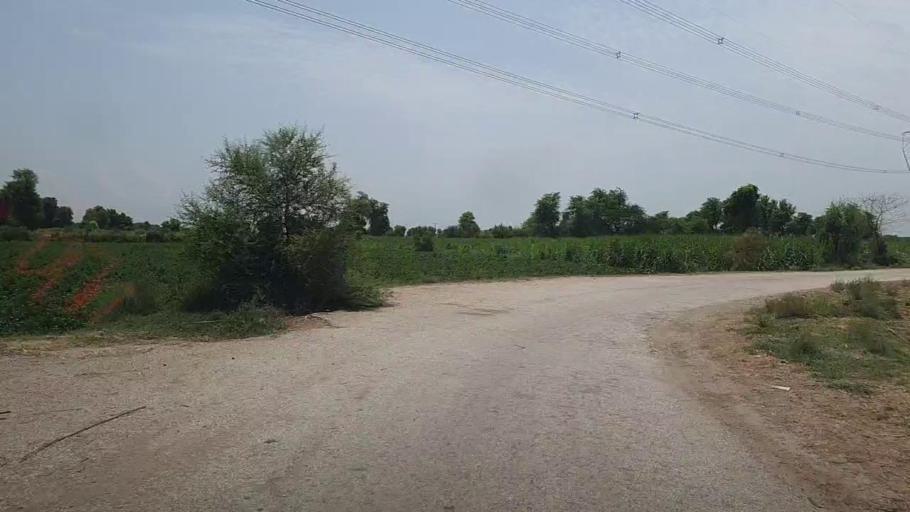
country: PK
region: Sindh
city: Pano Aqil
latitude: 27.8171
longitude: 69.2399
